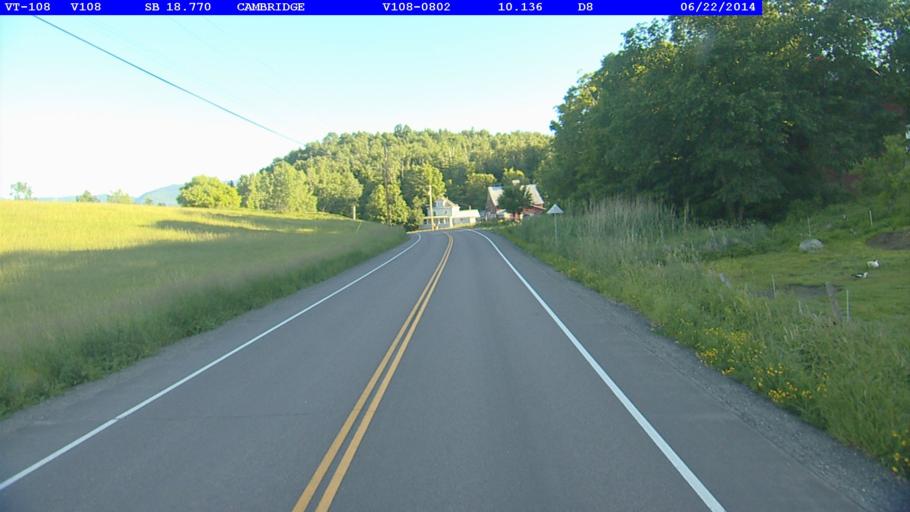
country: US
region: Vermont
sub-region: Lamoille County
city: Johnson
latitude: 44.6617
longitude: -72.8305
